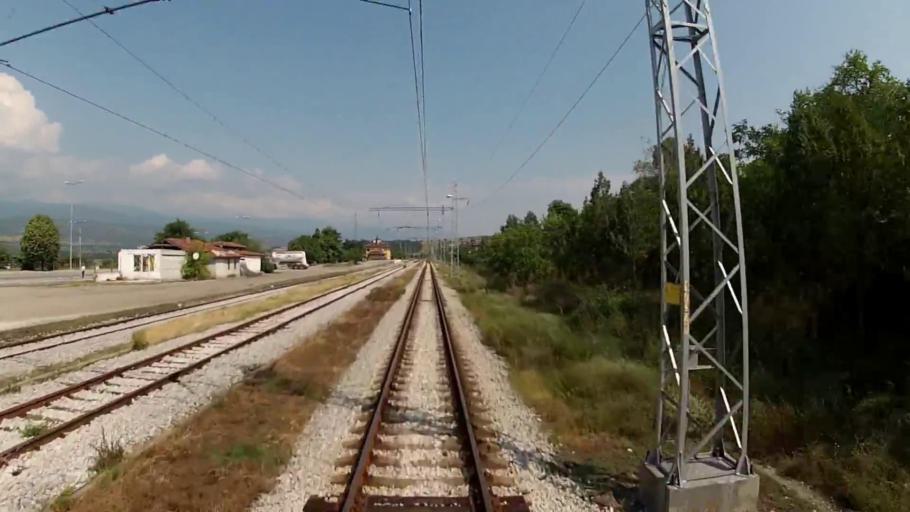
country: BG
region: Blagoevgrad
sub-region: Obshtina Strumyani
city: Strumyani
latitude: 41.6311
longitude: 23.2094
